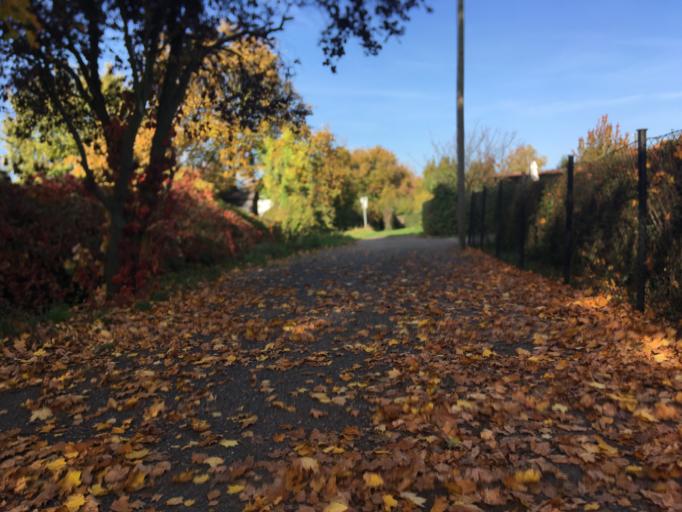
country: DE
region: Berlin
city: Rosenthal
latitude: 52.5942
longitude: 13.3897
